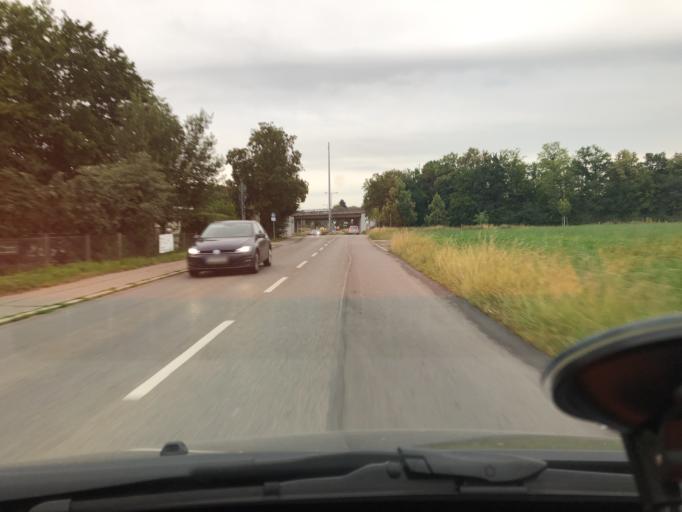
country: DE
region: Baden-Wuerttemberg
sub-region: Regierungsbezirk Stuttgart
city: Leinfelden-Echterdingen
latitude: 48.7357
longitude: 9.1623
